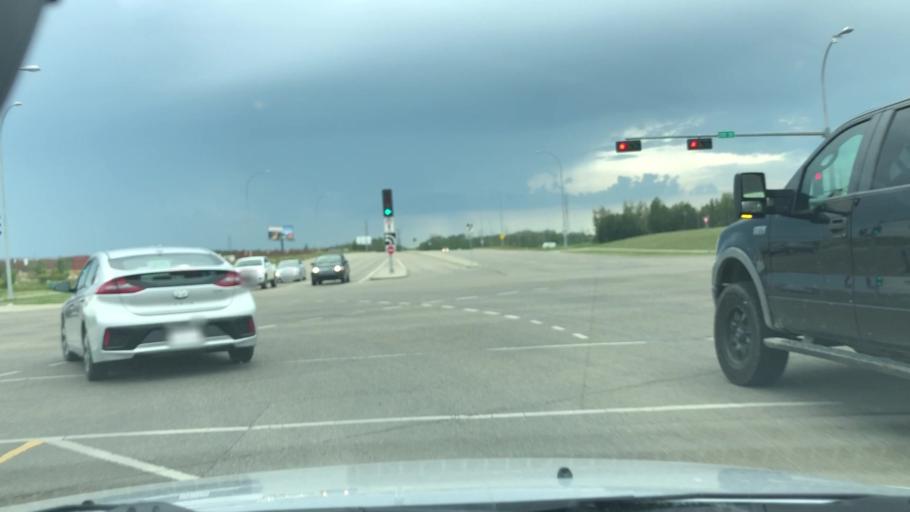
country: CA
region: Alberta
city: St. Albert
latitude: 53.5993
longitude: -113.6146
